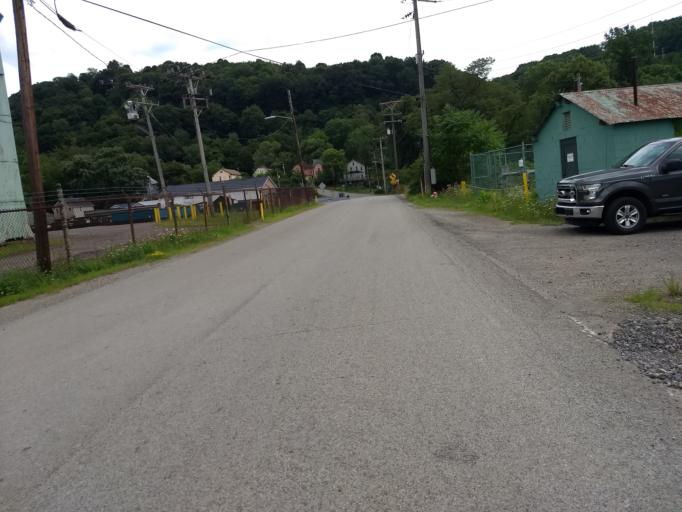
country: US
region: Pennsylvania
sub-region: Allegheny County
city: Brackenridge
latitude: 40.6129
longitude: -79.7148
